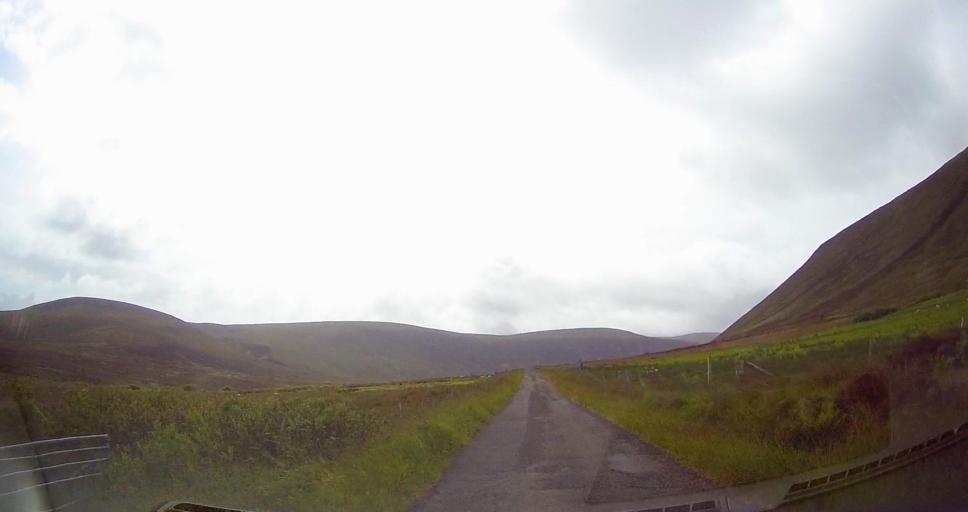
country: GB
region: Scotland
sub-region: Orkney Islands
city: Stromness
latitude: 58.9023
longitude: -3.3161
